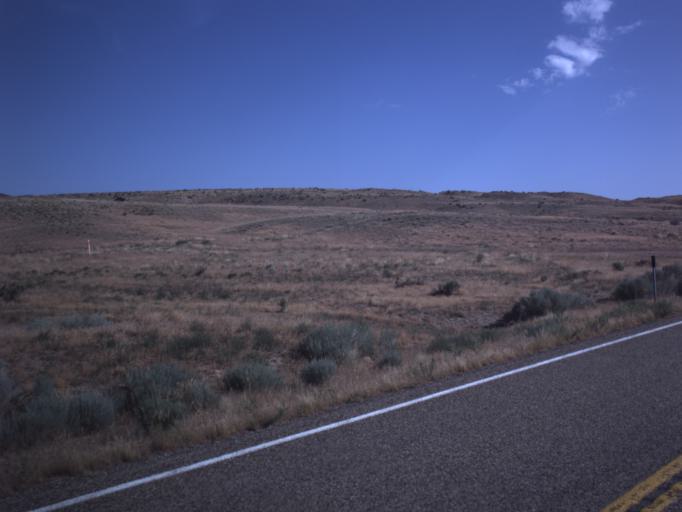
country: US
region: Utah
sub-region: Beaver County
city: Milford
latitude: 38.7625
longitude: -112.9403
